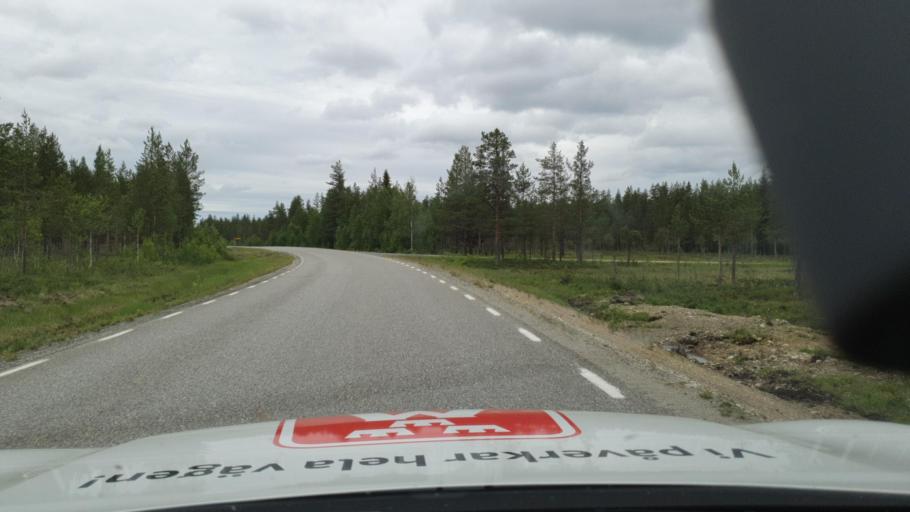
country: SE
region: Vaesterbotten
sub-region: Lycksele Kommun
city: Lycksele
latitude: 64.1835
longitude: 18.3151
